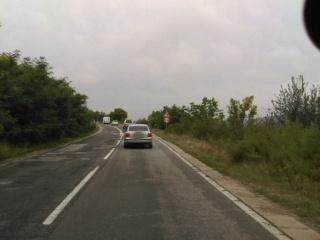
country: BG
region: Plovdiv
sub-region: Obshtina Karlovo
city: Karlovo
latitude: 42.5915
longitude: 24.8165
